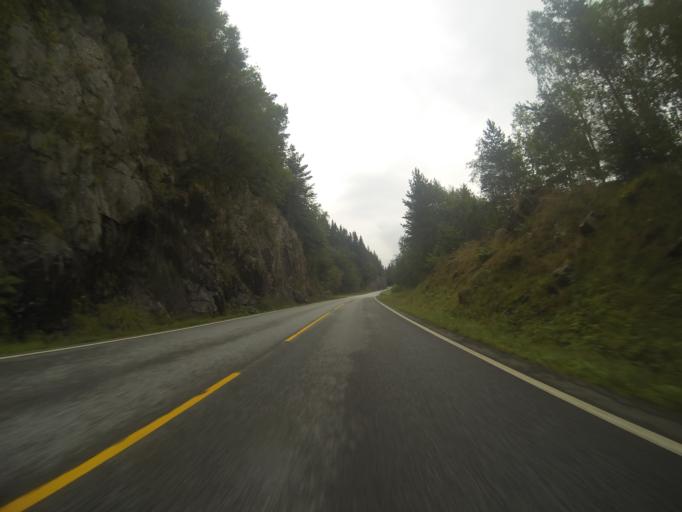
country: NO
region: Rogaland
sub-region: Suldal
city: Sand
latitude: 59.4894
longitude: 6.2016
